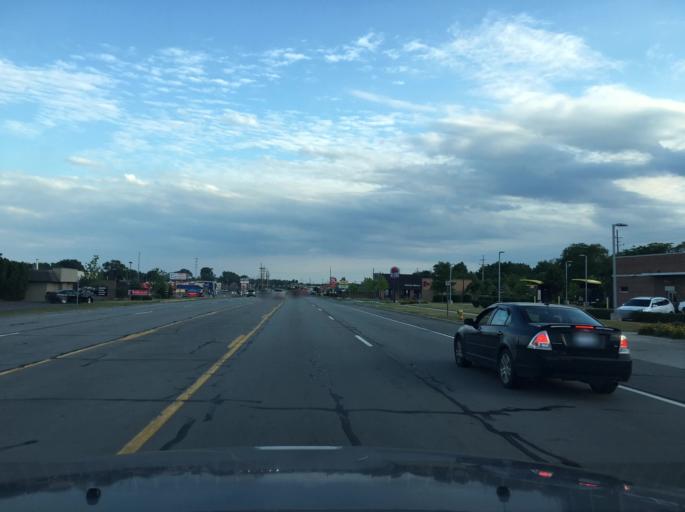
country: US
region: Michigan
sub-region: Macomb County
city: Mount Clemens
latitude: 42.6024
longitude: -82.8993
